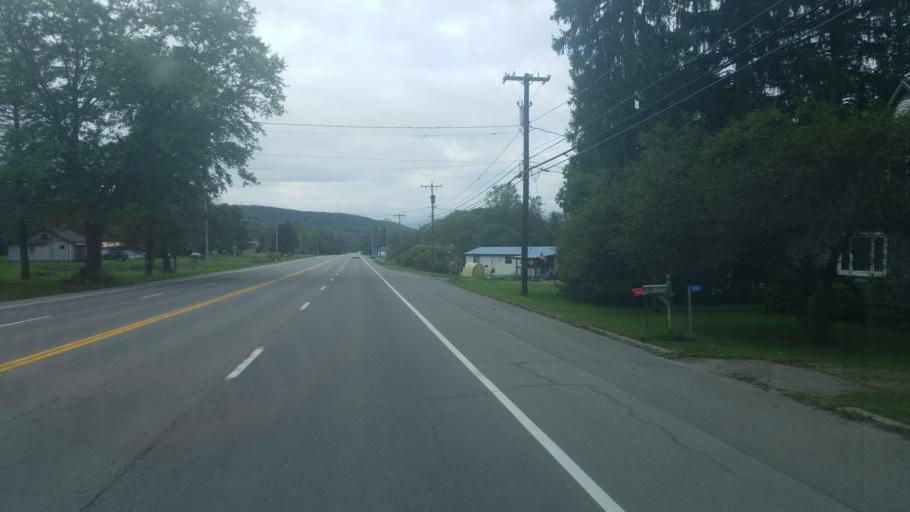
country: US
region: New York
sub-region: Cattaraugus County
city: Weston Mills
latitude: 42.1502
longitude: -78.3987
